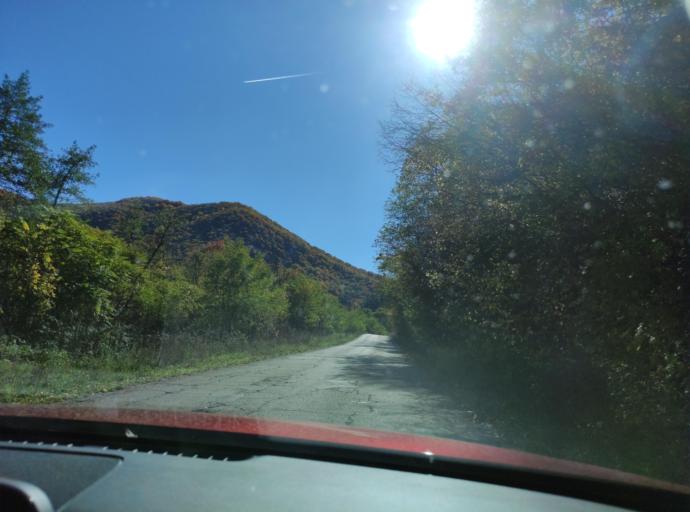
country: BG
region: Montana
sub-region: Obshtina Chiprovtsi
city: Chiprovtsi
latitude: 43.4083
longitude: 22.9386
